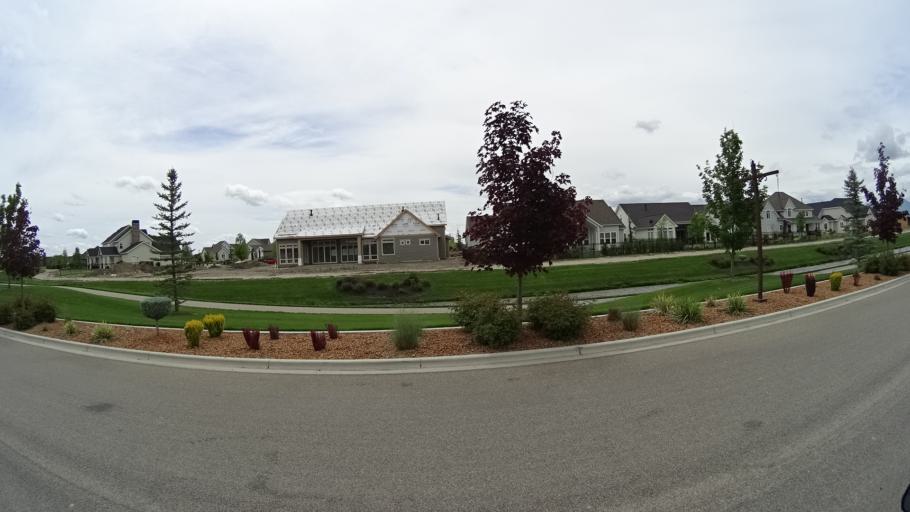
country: US
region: Idaho
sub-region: Ada County
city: Star
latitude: 43.7031
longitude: -116.4331
